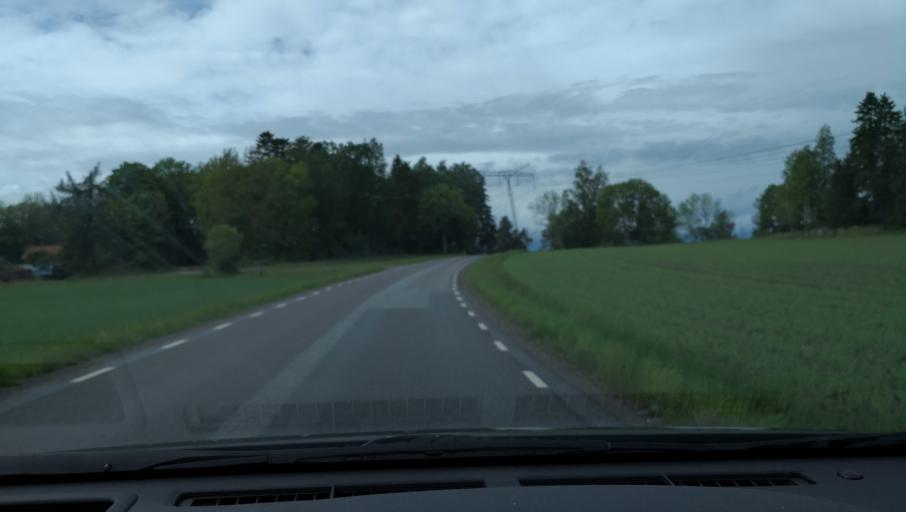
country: SE
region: Uppsala
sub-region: Enkopings Kommun
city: Orsundsbro
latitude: 59.6932
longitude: 17.3729
